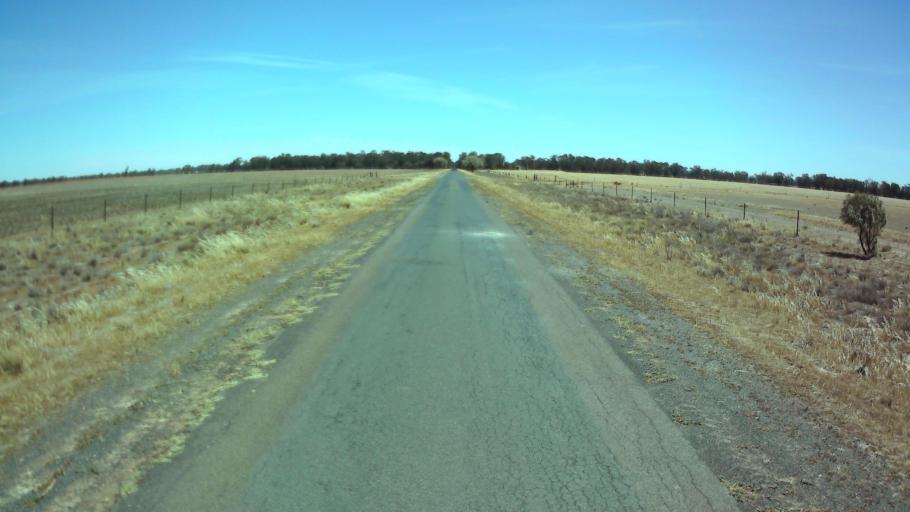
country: AU
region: New South Wales
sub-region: Weddin
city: Grenfell
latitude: -33.8602
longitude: 147.6939
